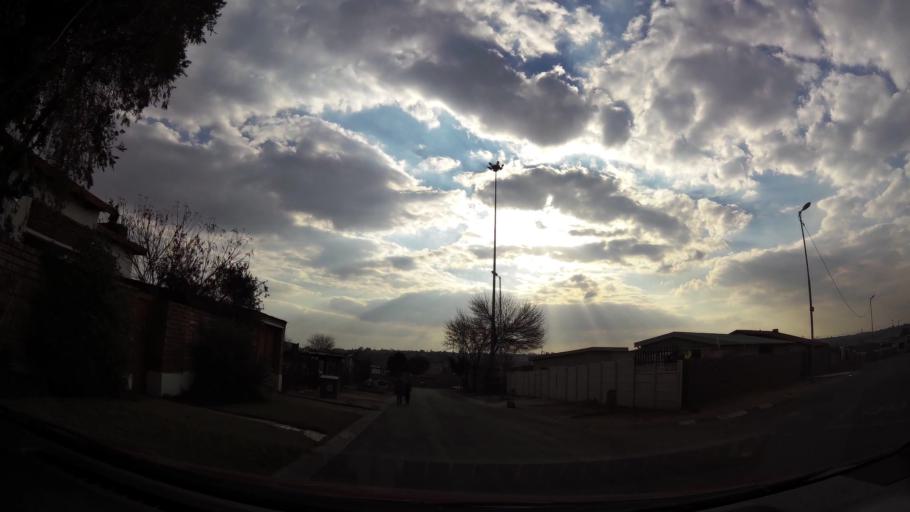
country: ZA
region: Gauteng
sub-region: City of Johannesburg Metropolitan Municipality
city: Soweto
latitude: -26.2432
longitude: 27.9162
